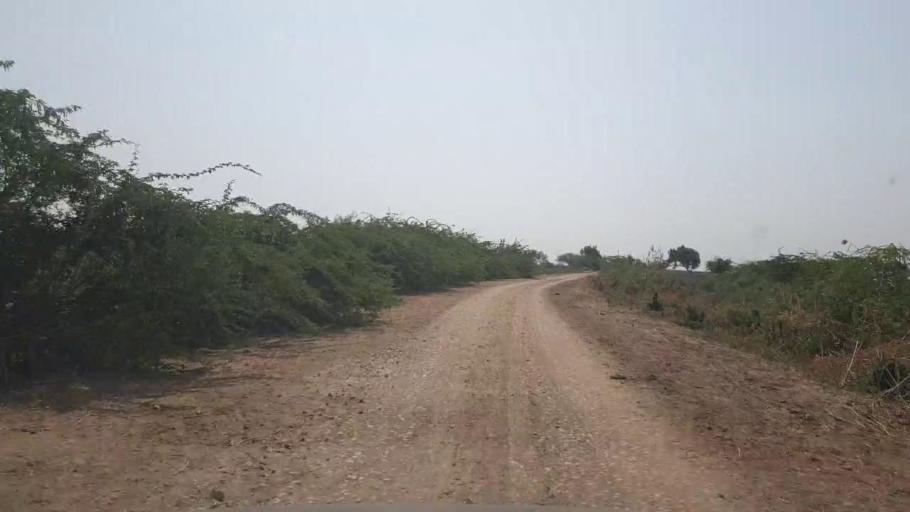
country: PK
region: Sindh
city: Jati
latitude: 24.3815
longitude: 68.6019
